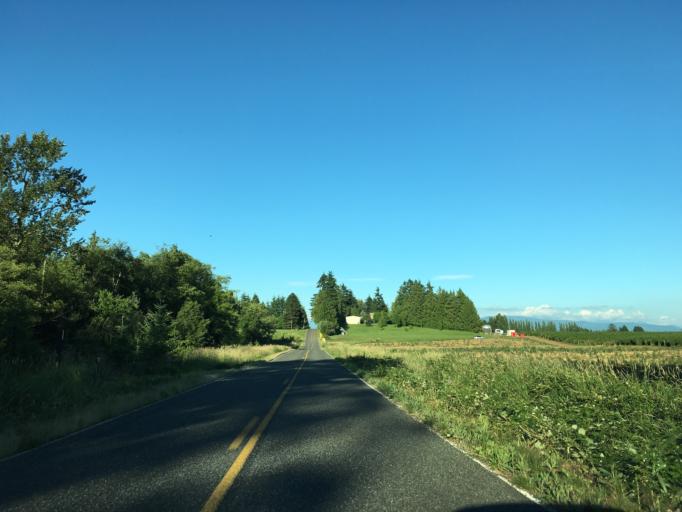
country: US
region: Washington
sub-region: Whatcom County
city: Lynden
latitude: 48.9829
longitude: -122.5235
